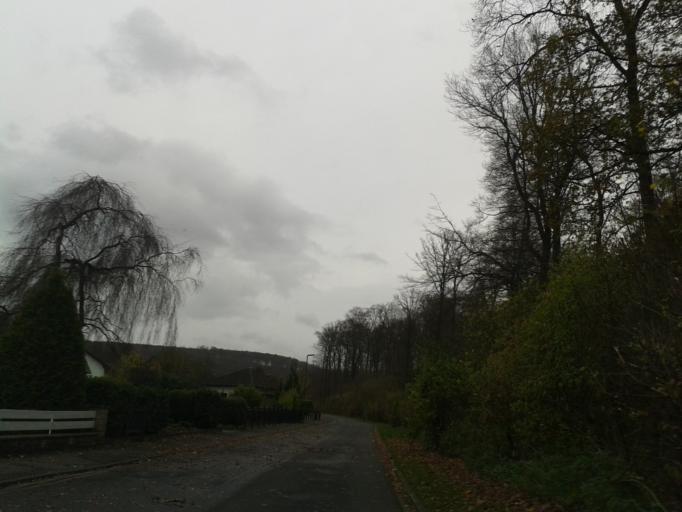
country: DE
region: North Rhine-Westphalia
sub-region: Regierungsbezirk Detmold
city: Schieder-Schwalenberg
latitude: 51.9091
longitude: 9.1520
